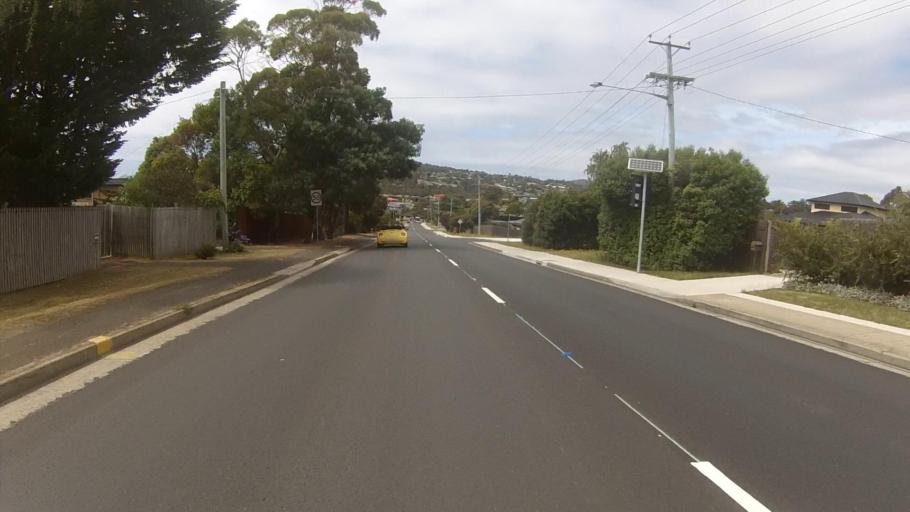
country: AU
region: Tasmania
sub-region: Kingborough
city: Kingston
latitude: -42.9698
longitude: 147.2913
